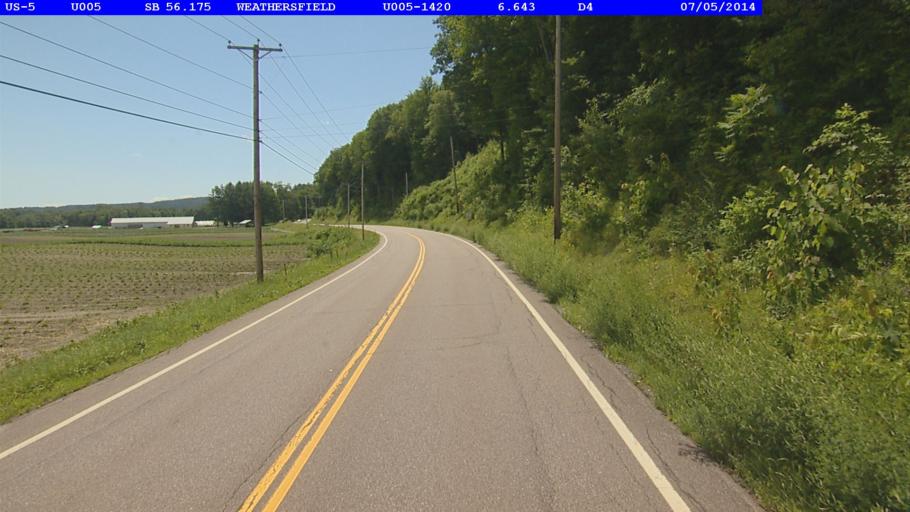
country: US
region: Vermont
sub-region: Windsor County
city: Windsor
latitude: 43.4272
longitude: -72.4005
